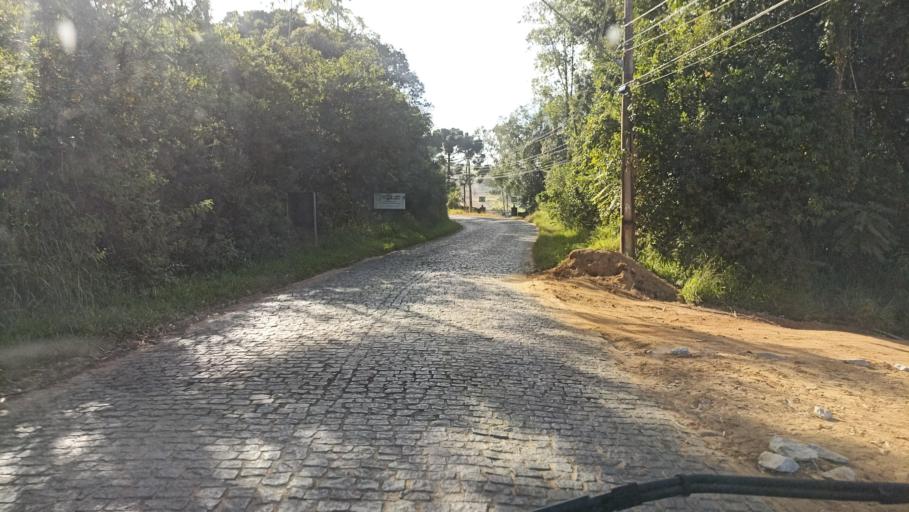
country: BR
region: Minas Gerais
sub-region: Tiradentes
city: Tiradentes
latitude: -21.1208
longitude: -44.1914
